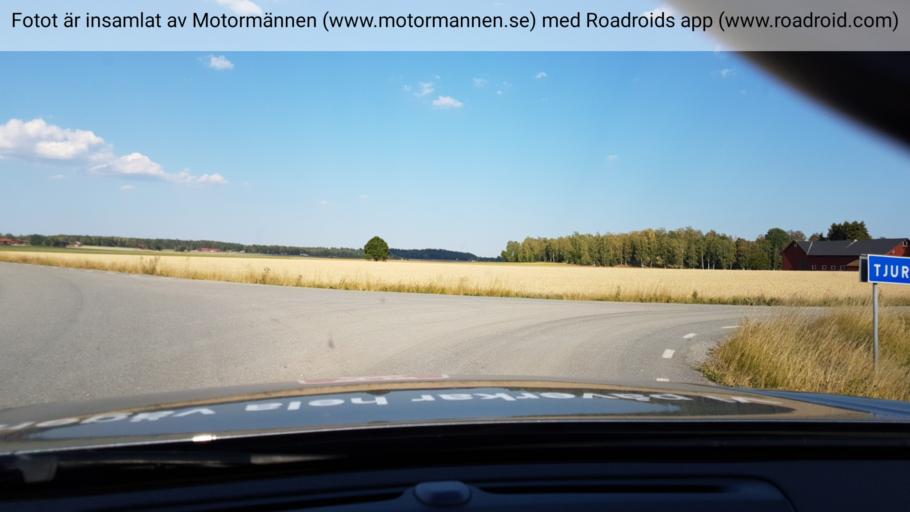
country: SE
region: Uppsala
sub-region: Enkopings Kommun
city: Enkoping
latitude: 59.7067
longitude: 17.0398
